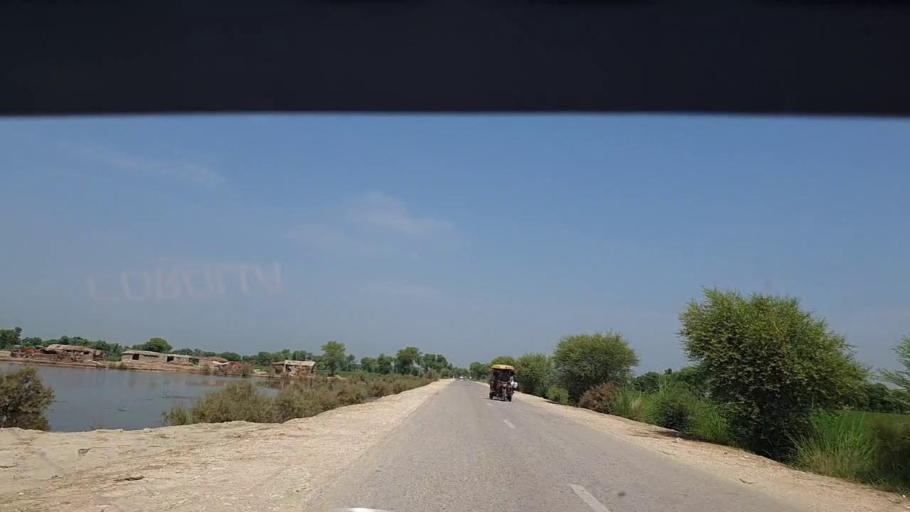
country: PK
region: Sindh
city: Thul
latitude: 28.1396
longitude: 68.8175
